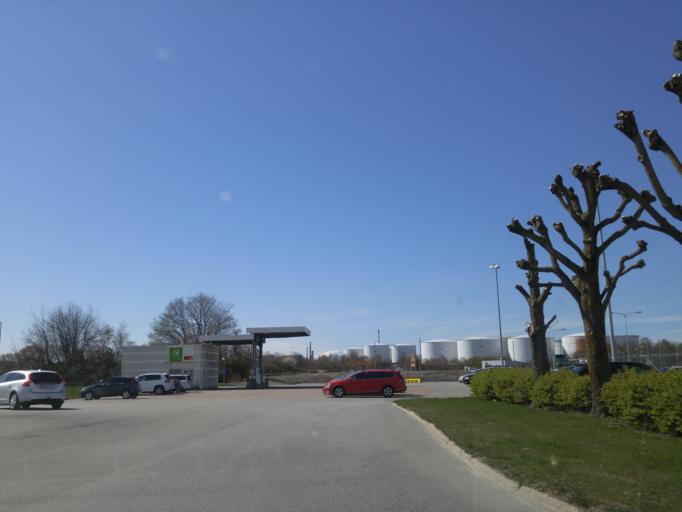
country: SE
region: Vaestra Goetaland
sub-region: Goteborg
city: Torslanda
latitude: 57.7140
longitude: 11.8429
